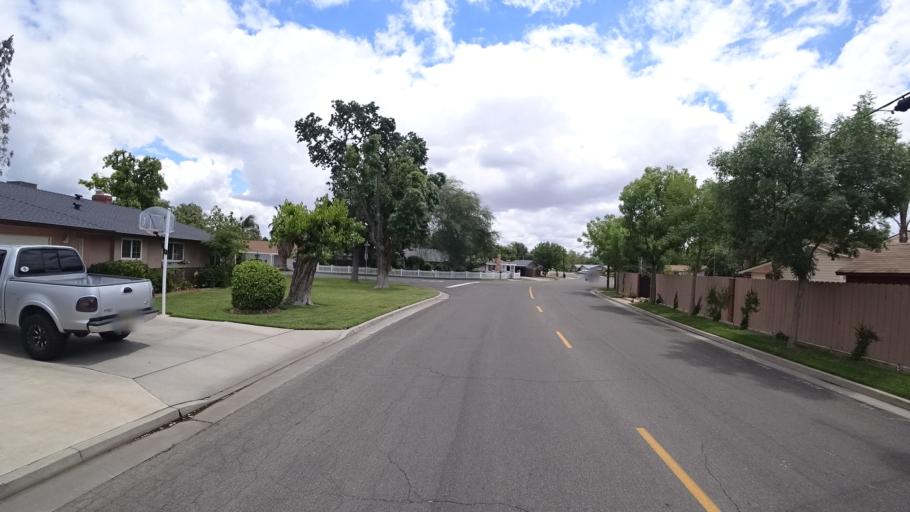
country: US
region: California
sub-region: Kings County
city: Hanford
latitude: 36.3445
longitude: -119.6524
